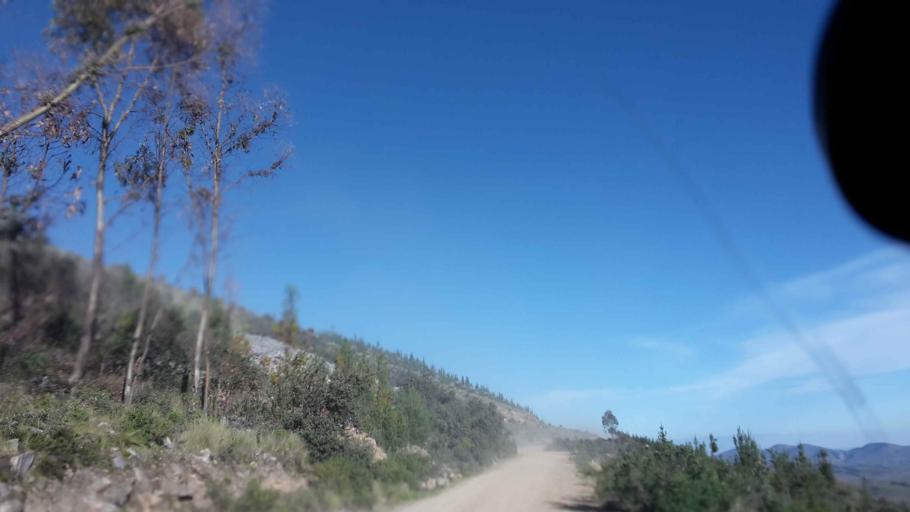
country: BO
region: Cochabamba
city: Arani
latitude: -17.7177
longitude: -65.6584
